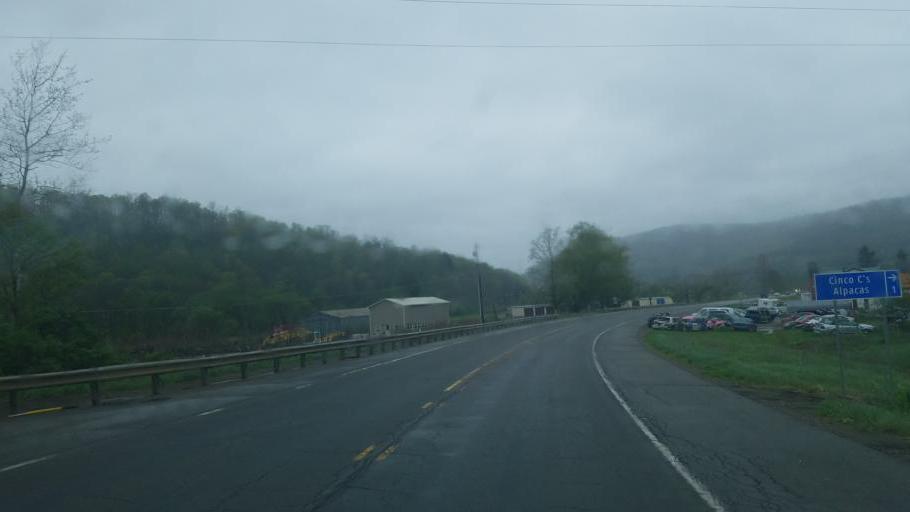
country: US
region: Pennsylvania
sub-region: McKean County
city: Port Allegany
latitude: 41.7870
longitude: -78.2028
